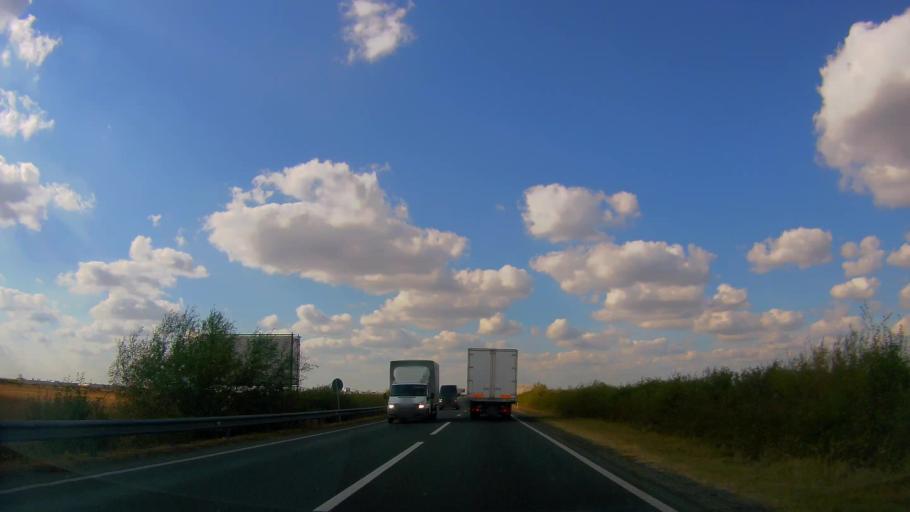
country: RO
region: Satu Mare
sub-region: Oras Ardud
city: Madaras
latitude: 47.7244
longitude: 22.8873
